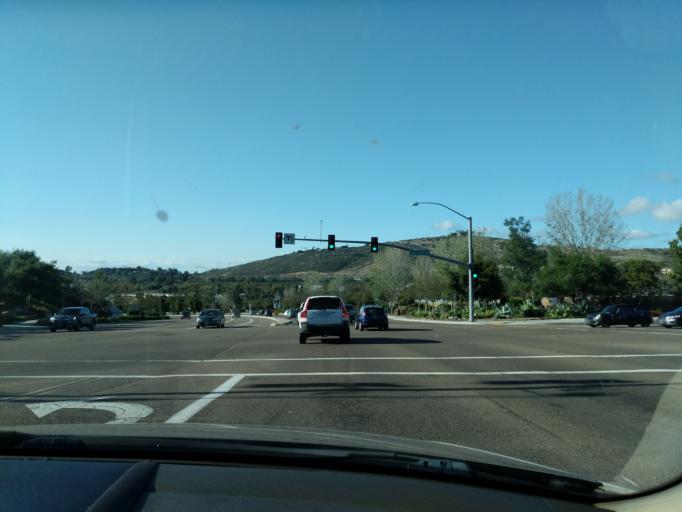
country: US
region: California
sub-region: San Diego County
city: Lake San Marcos
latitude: 33.0997
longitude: -117.2219
